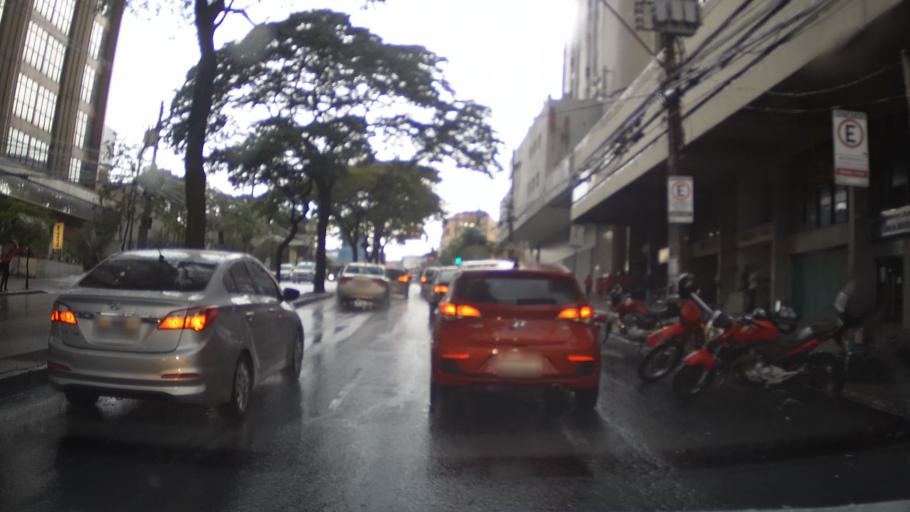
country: BR
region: Minas Gerais
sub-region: Belo Horizonte
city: Belo Horizonte
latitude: -19.9486
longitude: -43.9611
